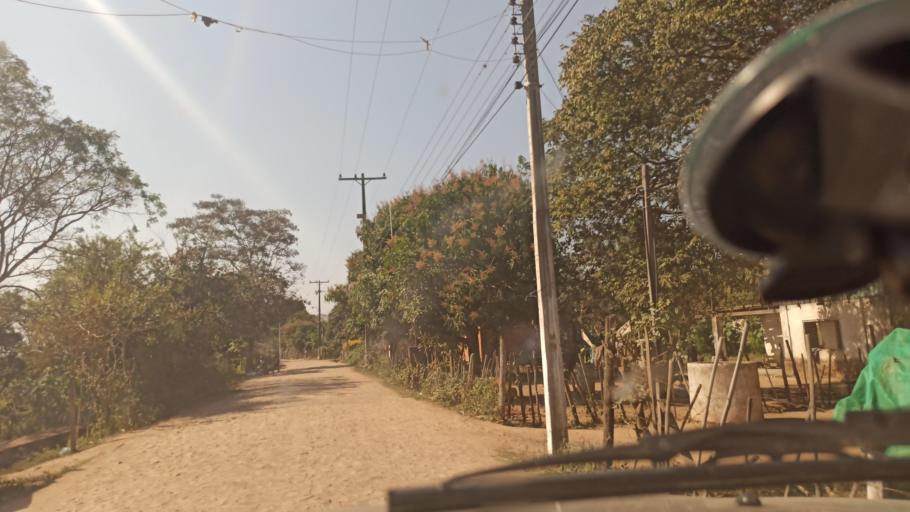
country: AR
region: Formosa
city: Clorinda
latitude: -25.2948
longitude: -57.6987
